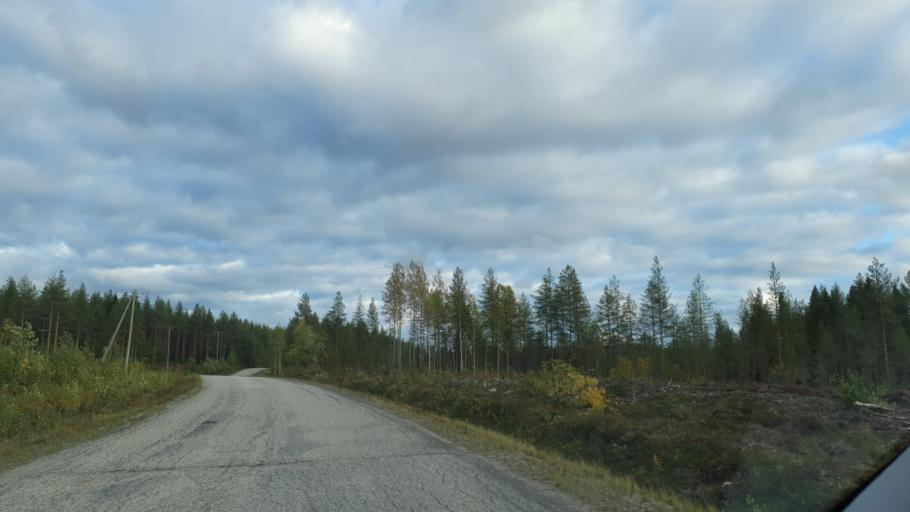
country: FI
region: North Karelia
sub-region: Pielisen Karjala
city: Lieksa
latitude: 63.9149
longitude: 30.1810
